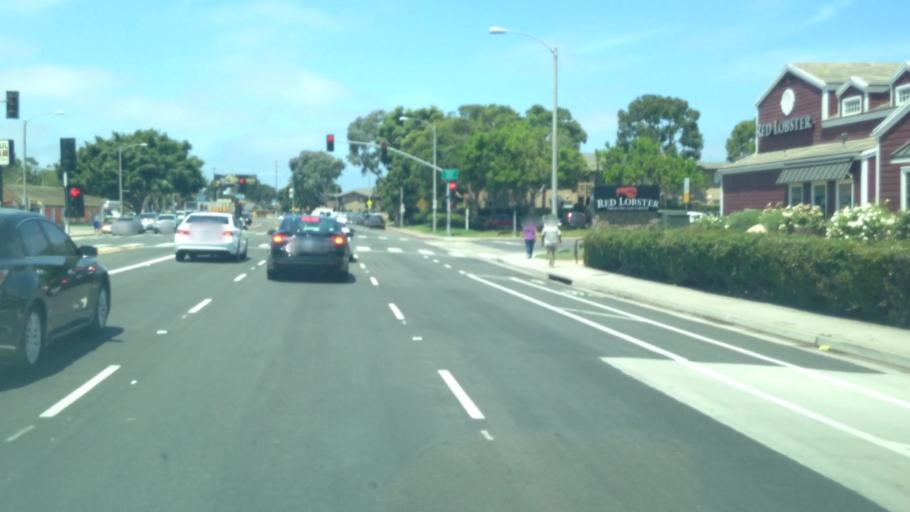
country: US
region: California
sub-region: San Diego County
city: San Diego
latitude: 32.7546
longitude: -117.2165
